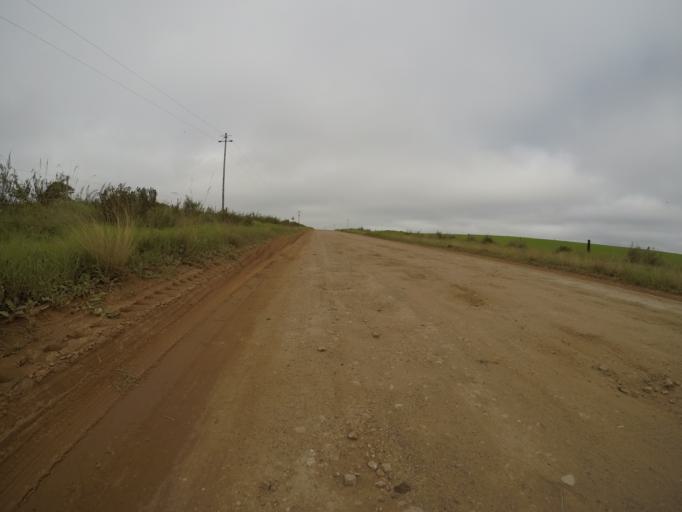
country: ZA
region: Eastern Cape
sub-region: Cacadu District Municipality
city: Kareedouw
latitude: -34.0221
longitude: 24.2403
